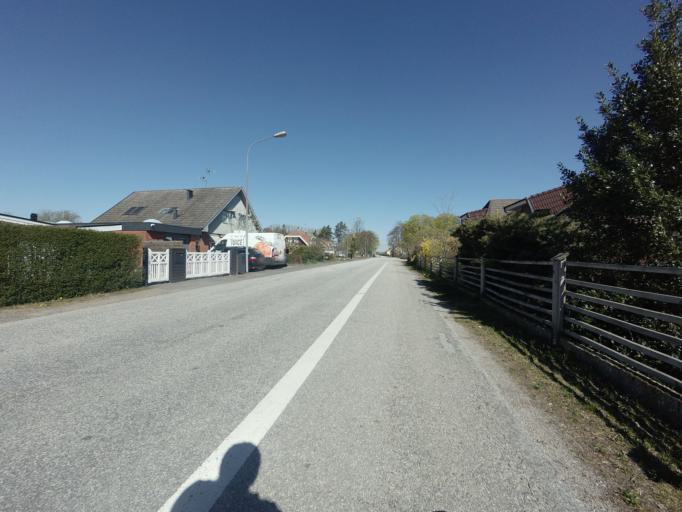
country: SE
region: Skane
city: Bjarred
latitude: 55.7370
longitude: 13.0317
